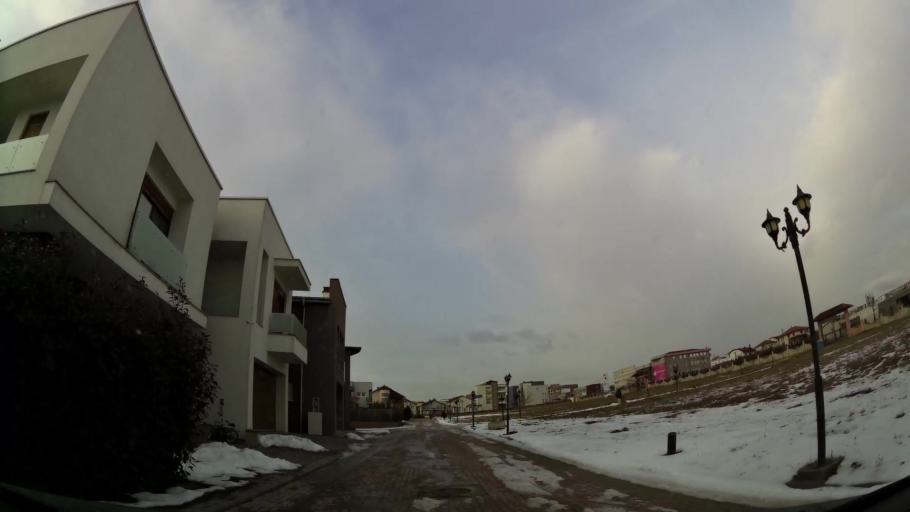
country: XK
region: Pristina
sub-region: Komuna e Prishtines
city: Pristina
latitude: 42.6231
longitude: 21.1603
